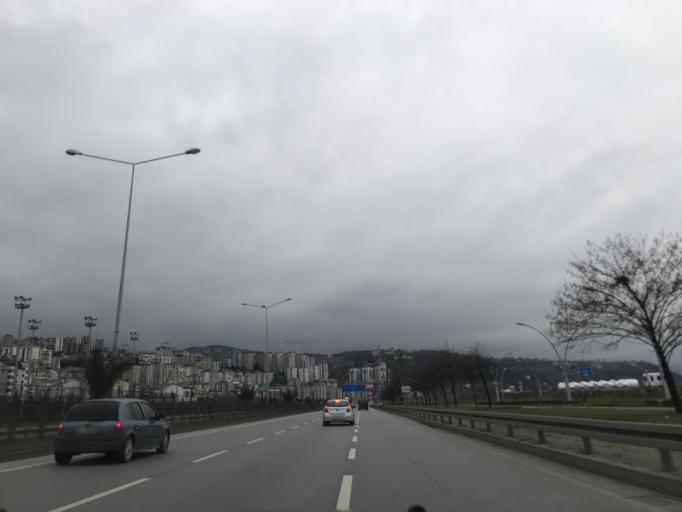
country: TR
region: Trabzon
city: Trabzon
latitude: 40.9975
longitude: 39.6718
